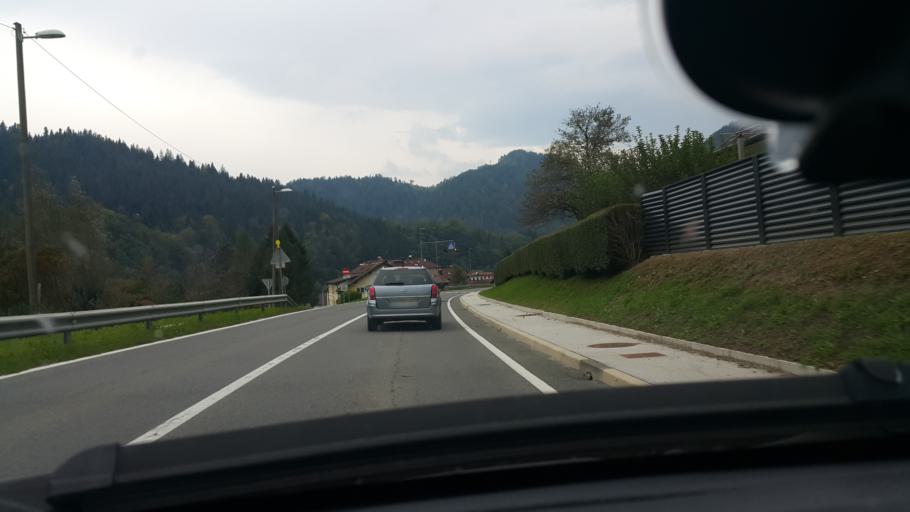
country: SI
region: Podvelka
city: Podvelka
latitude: 46.5907
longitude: 15.3218
